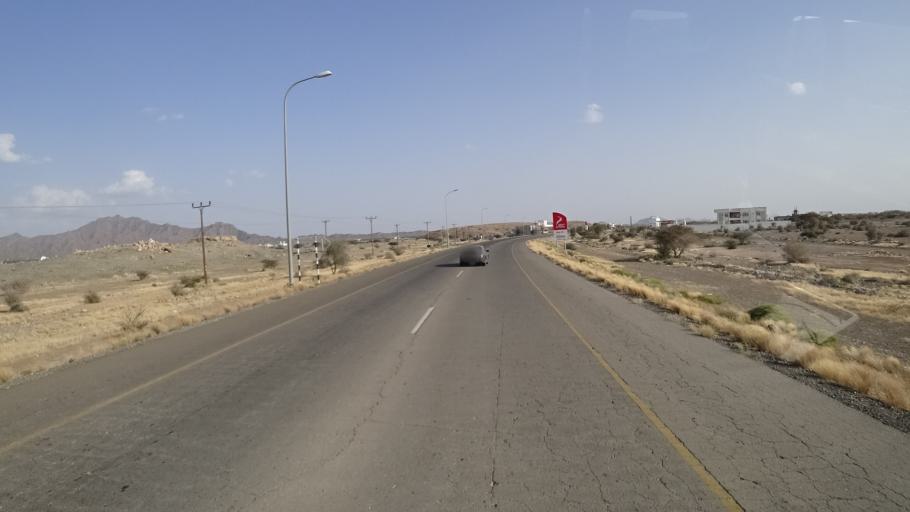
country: OM
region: Muhafazat ad Dakhiliyah
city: Izki
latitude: 22.8985
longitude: 57.7488
